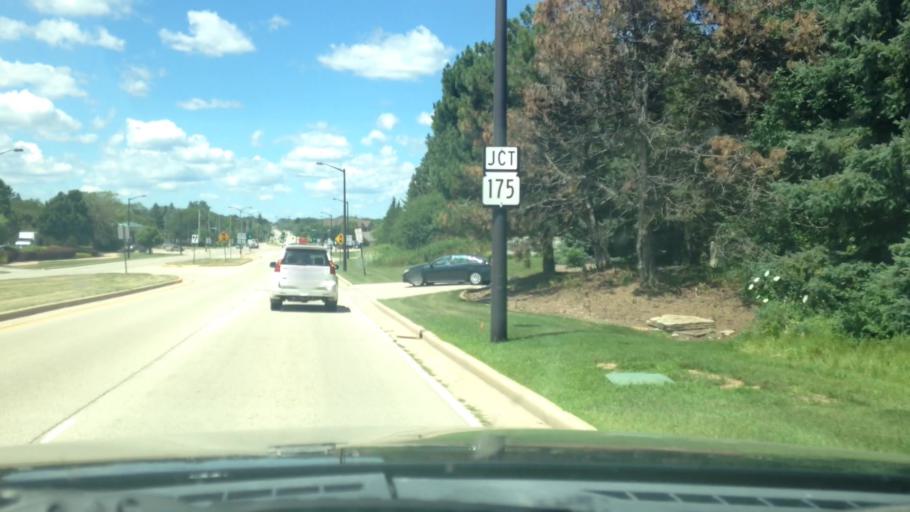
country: US
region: Wisconsin
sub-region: Waukesha County
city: Butler
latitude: 43.1483
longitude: -88.0706
